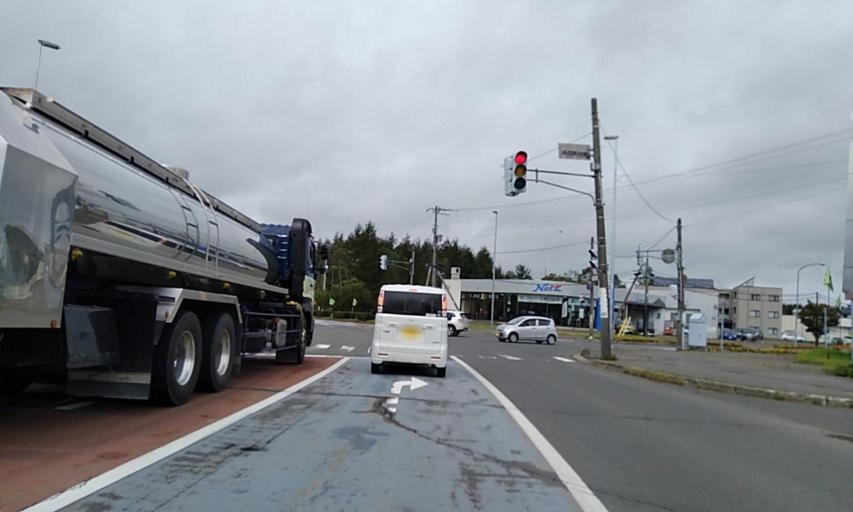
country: JP
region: Hokkaido
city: Bihoro
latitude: 43.4928
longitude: 144.4544
